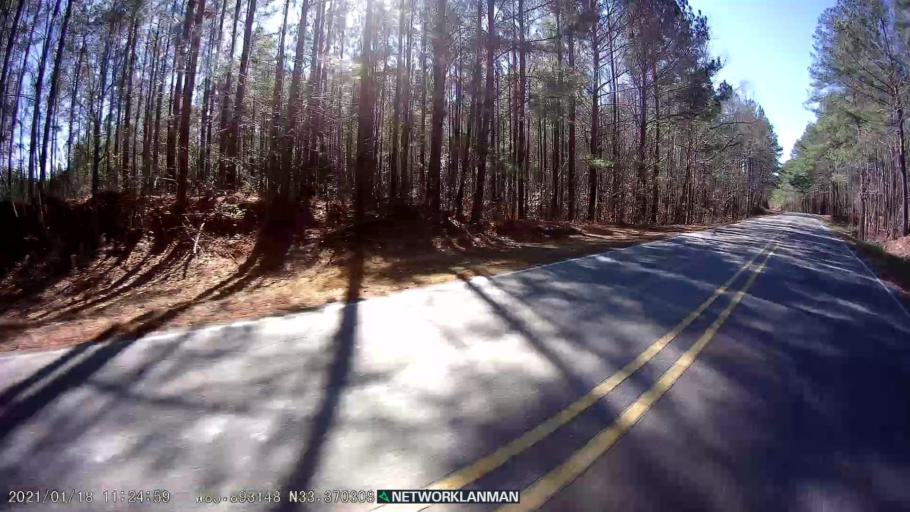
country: US
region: Alabama
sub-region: Clay County
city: Ashland
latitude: 33.3702
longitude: -85.8935
